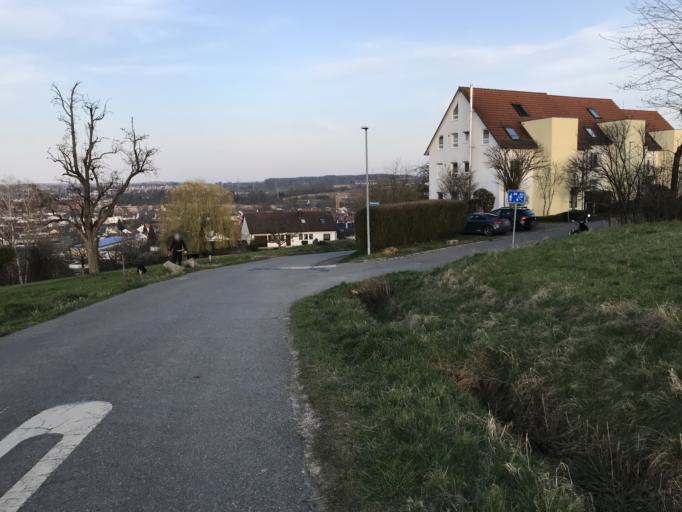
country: DE
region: Baden-Wuerttemberg
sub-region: Regierungsbezirk Stuttgart
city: Unterensingen
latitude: 48.6594
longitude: 9.3500
